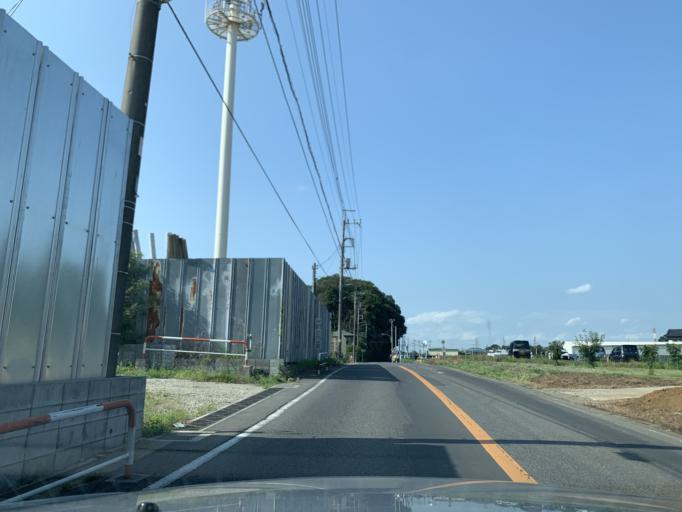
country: JP
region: Chiba
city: Nagareyama
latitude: 35.8460
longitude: 139.9344
